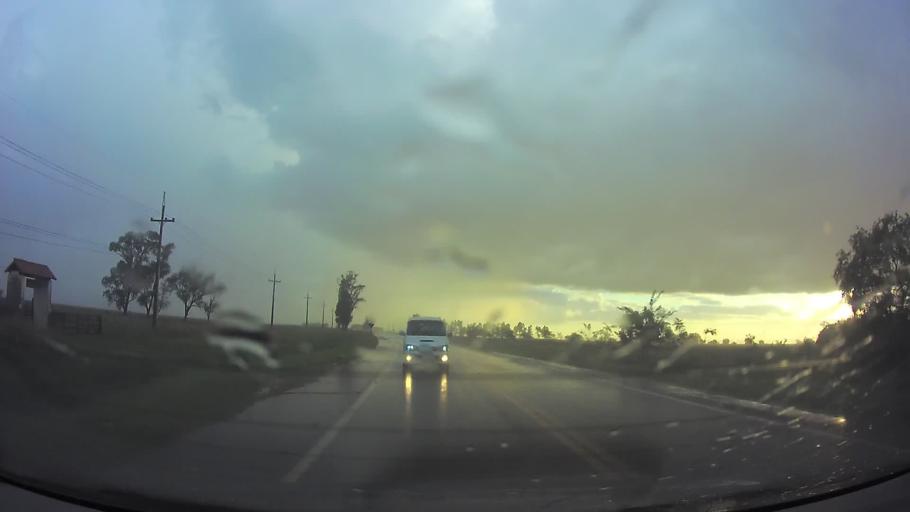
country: PY
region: Paraguari
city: Paraguari
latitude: -25.6467
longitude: -57.1584
